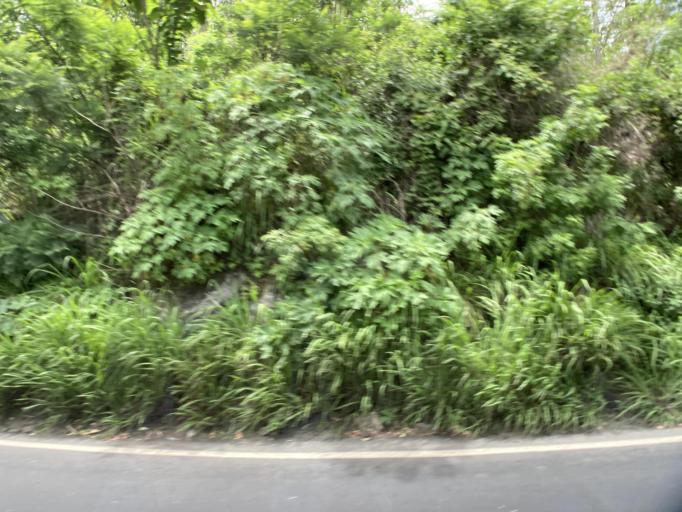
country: GT
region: Guatemala
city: Amatitlan
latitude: 14.4995
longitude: -90.6261
